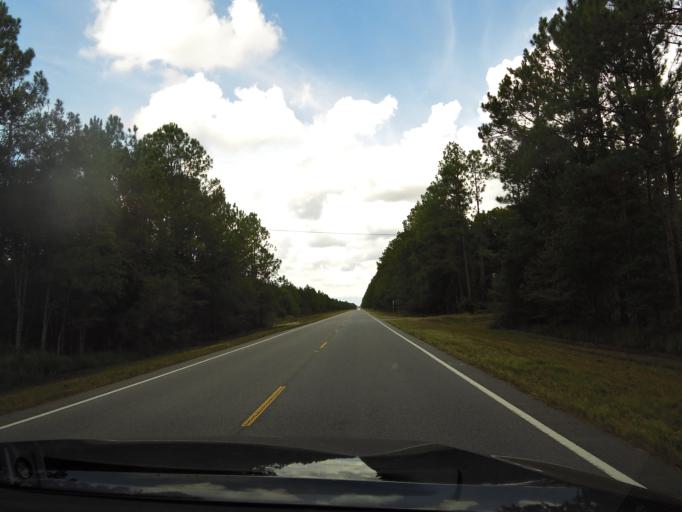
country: US
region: Georgia
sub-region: Charlton County
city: Folkston
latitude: 30.9589
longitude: -82.0237
